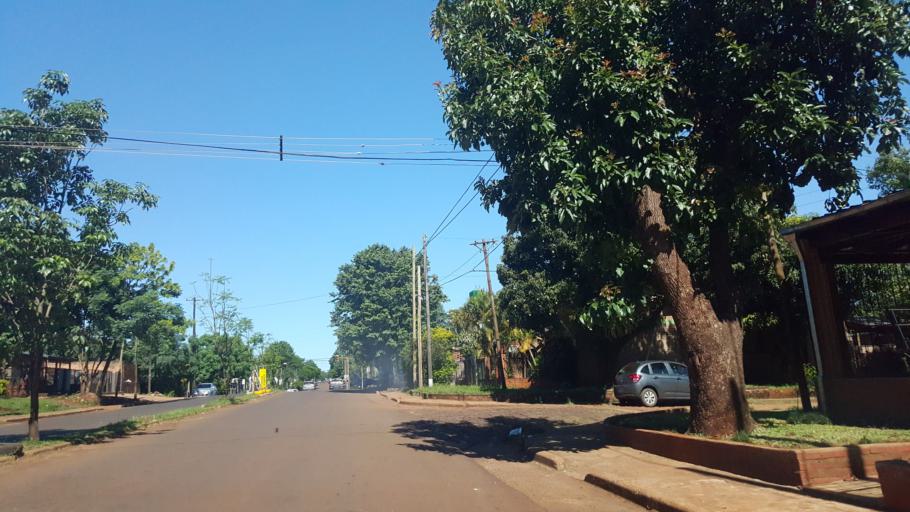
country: AR
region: Misiones
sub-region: Departamento de Capital
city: Posadas
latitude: -27.3888
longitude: -55.9208
